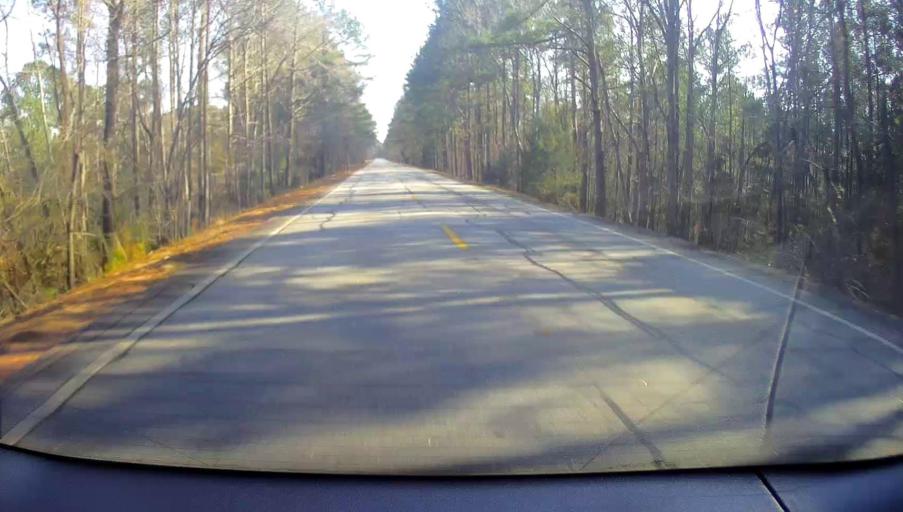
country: US
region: Georgia
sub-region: Butts County
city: Indian Springs
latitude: 33.2212
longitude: -83.8689
